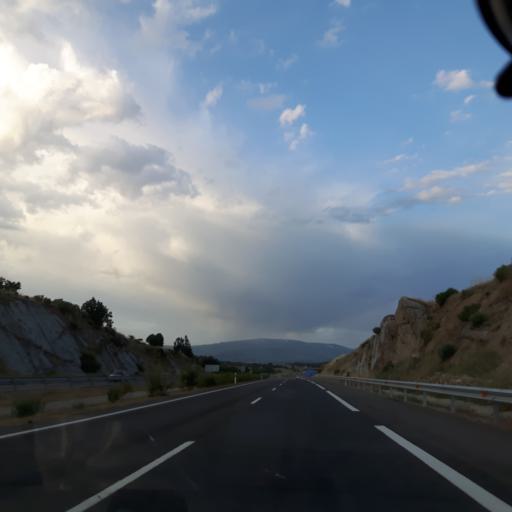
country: ES
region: Castille and Leon
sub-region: Provincia de Salamanca
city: Fuentes de Bejar
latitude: 40.5144
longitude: -5.6738
